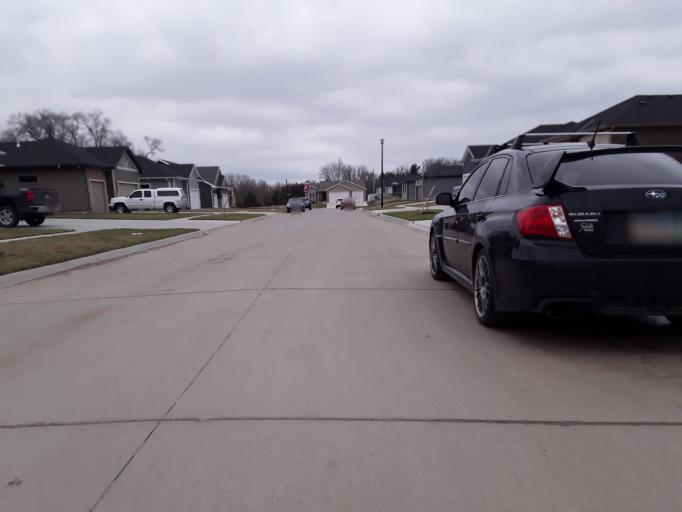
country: US
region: Nebraska
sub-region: Lancaster County
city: Lincoln
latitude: 40.8442
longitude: -96.5922
